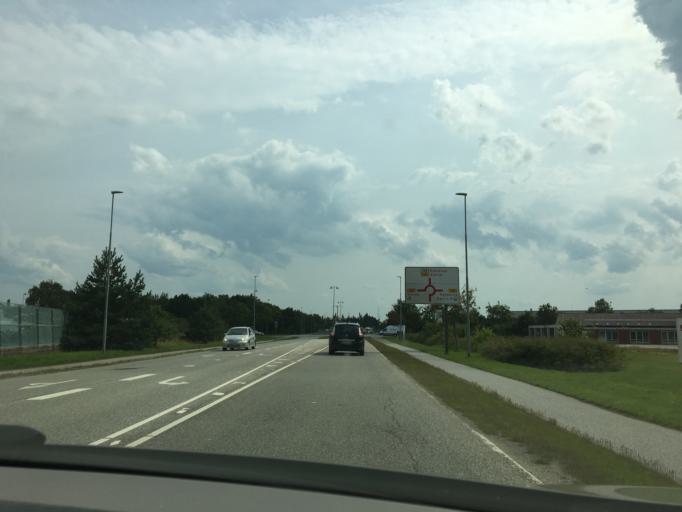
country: DK
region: Central Jutland
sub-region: Skive Kommune
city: Skive
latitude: 56.5449
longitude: 9.0312
